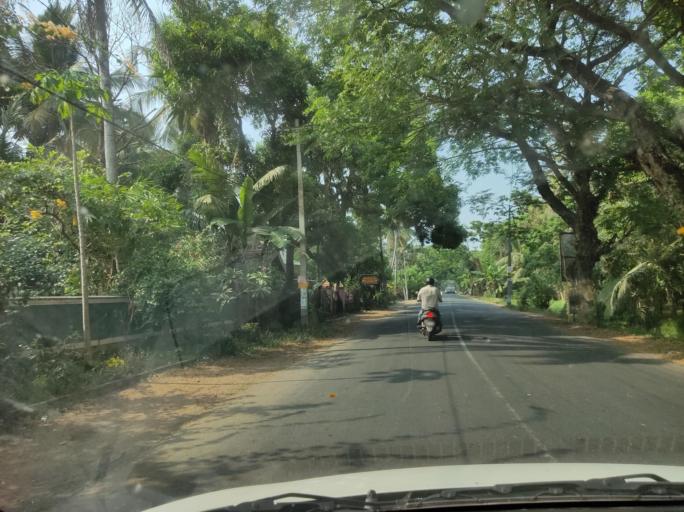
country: IN
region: Kerala
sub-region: Kottayam
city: Kottayam
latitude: 9.6204
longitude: 76.4304
